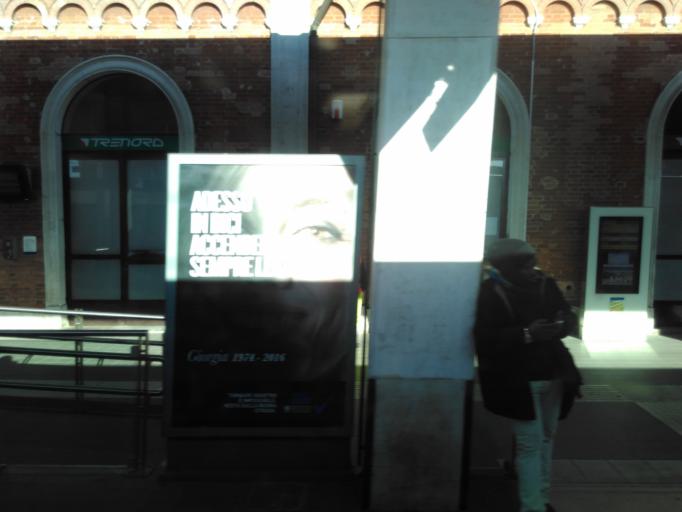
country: IT
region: Lombardy
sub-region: Provincia di Brescia
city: Brescia
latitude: 45.5326
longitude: 10.2119
